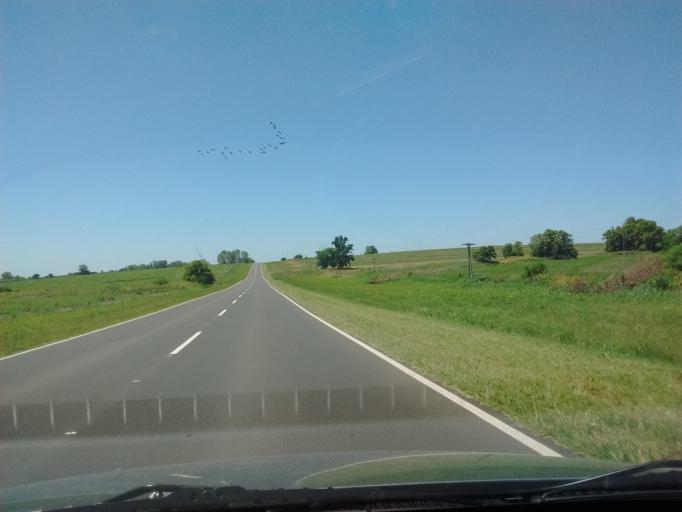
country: AR
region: Entre Rios
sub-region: Departamento de Victoria
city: Victoria
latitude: -32.8197
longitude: -59.8802
